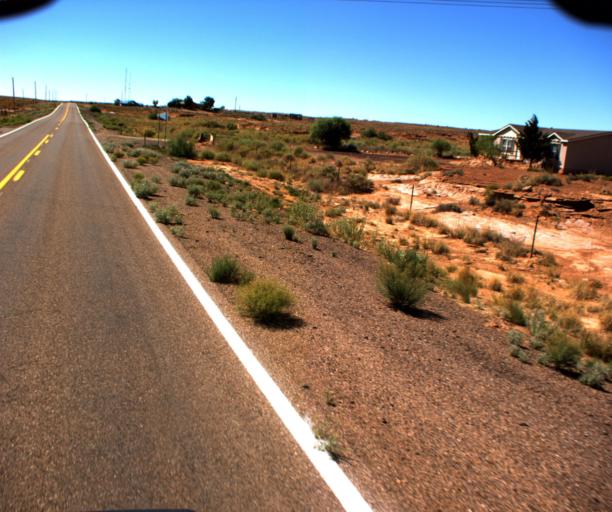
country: US
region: Arizona
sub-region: Navajo County
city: Winslow
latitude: 34.9839
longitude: -110.6615
